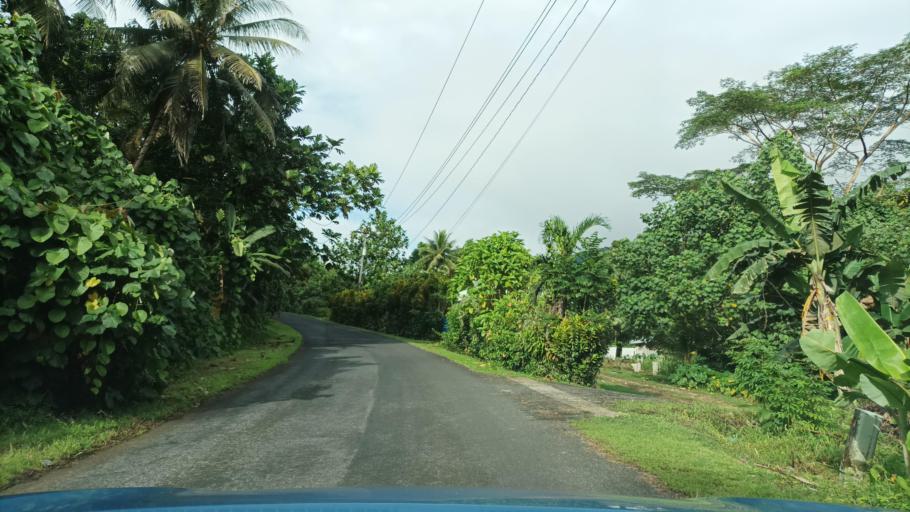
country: FM
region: Pohnpei
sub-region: Sokehs Municipality
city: Palikir - National Government Center
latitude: 6.9032
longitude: 158.1586
